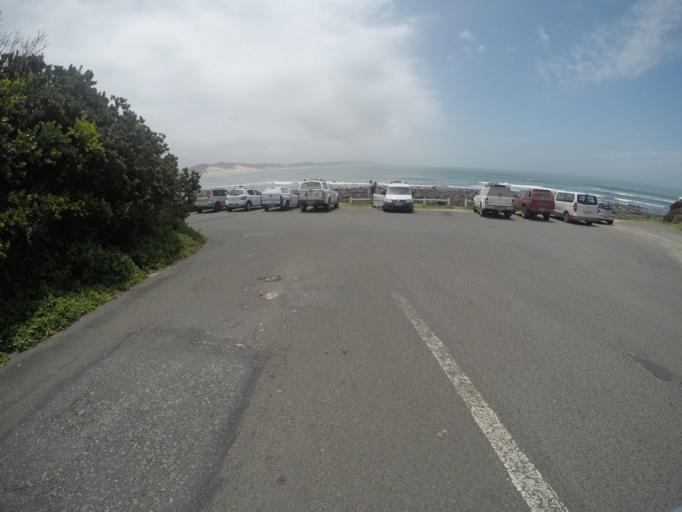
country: ZA
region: Eastern Cape
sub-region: Buffalo City Metropolitan Municipality
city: East London
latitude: -32.9961
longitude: 27.9511
